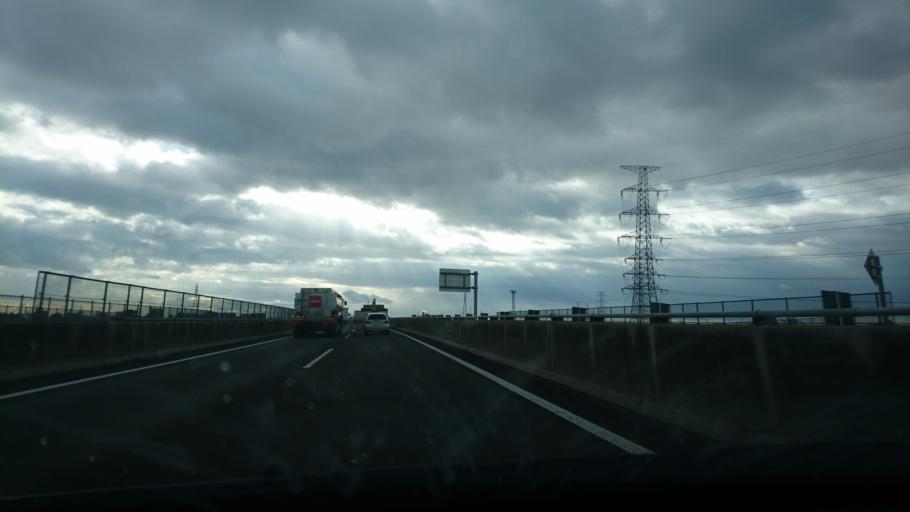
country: JP
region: Miyagi
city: Rifu
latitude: 38.3027
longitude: 140.9810
